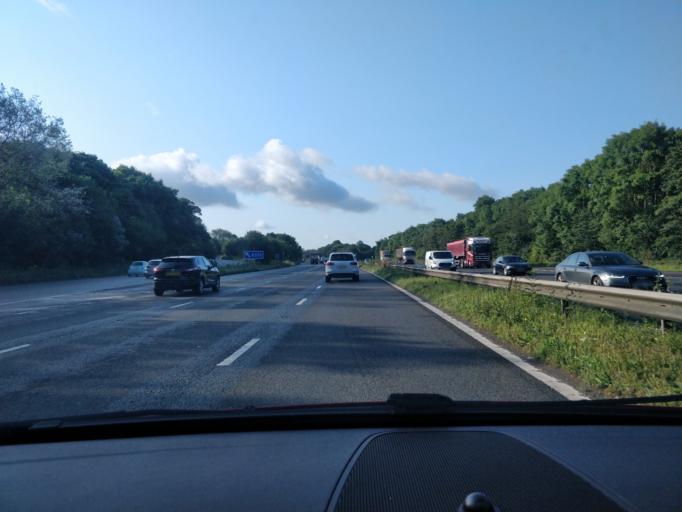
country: GB
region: England
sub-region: Knowsley
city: Knowsley
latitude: 53.4389
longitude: -2.8572
